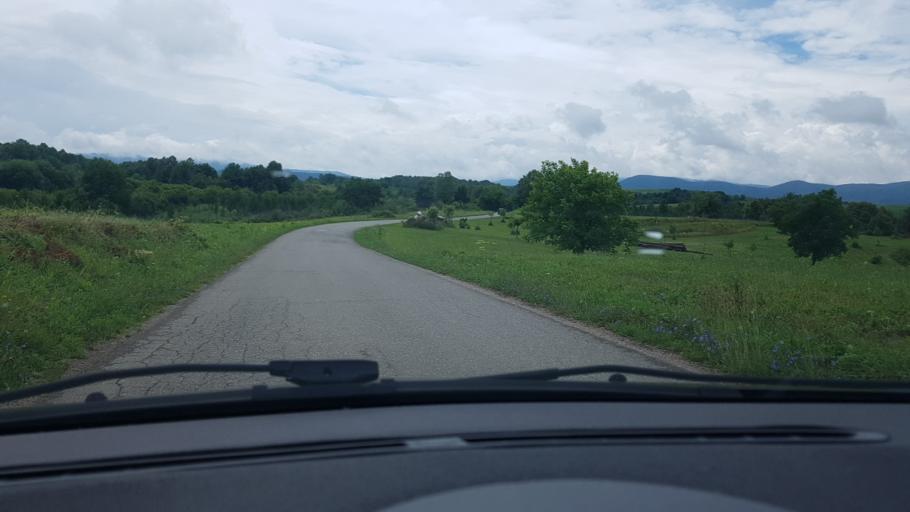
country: BA
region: Federation of Bosnia and Herzegovina
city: Trzacka Rastela
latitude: 44.9689
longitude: 15.6909
